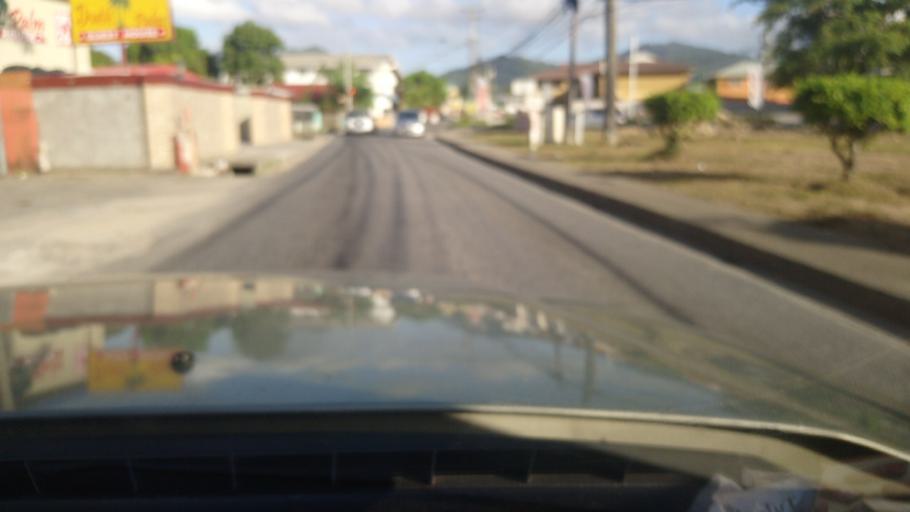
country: TT
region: Borough of Arima
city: Arima
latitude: 10.6300
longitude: -61.2754
